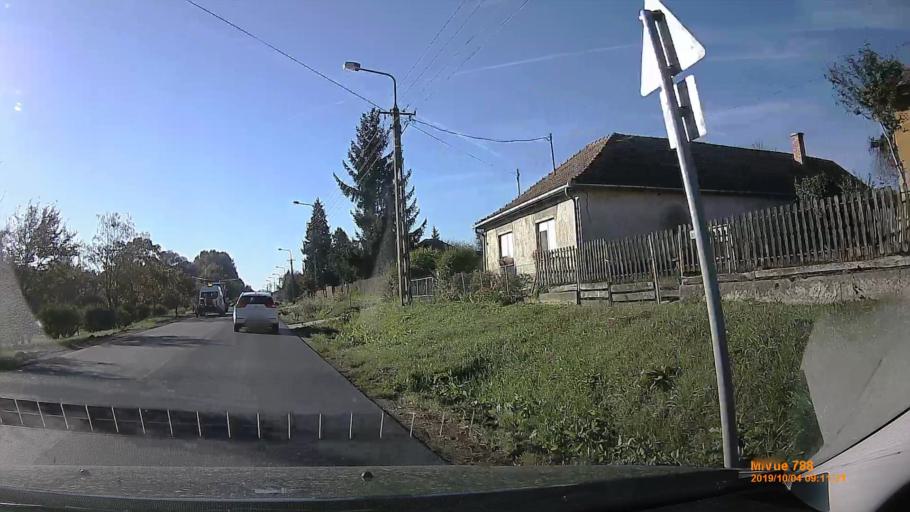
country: HU
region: Somogy
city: Karad
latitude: 46.6614
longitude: 17.7813
